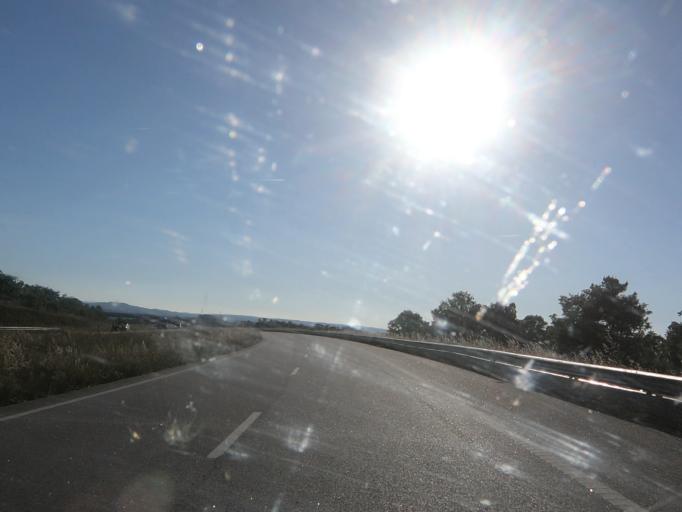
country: PT
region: Guarda
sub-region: Pinhel
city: Pinhel
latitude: 40.6108
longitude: -7.0037
